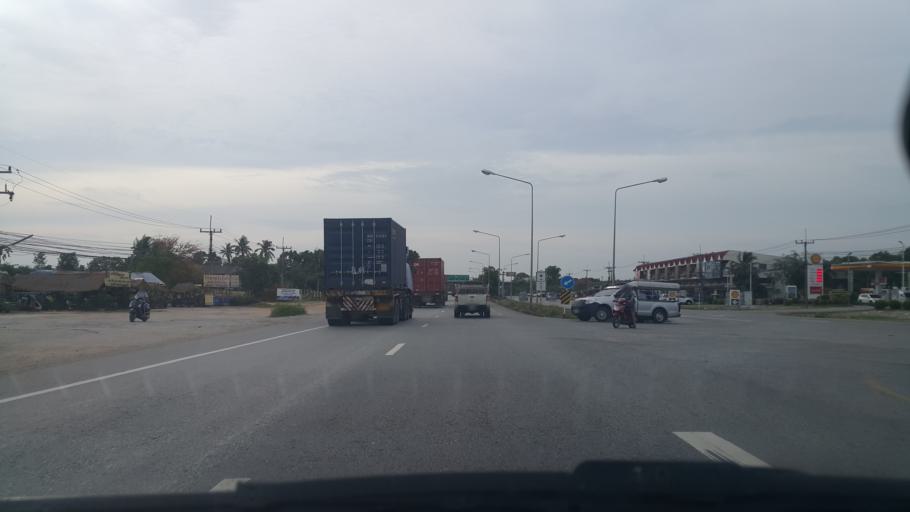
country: TH
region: Chon Buri
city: Bang Lamung
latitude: 12.9951
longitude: 100.9363
